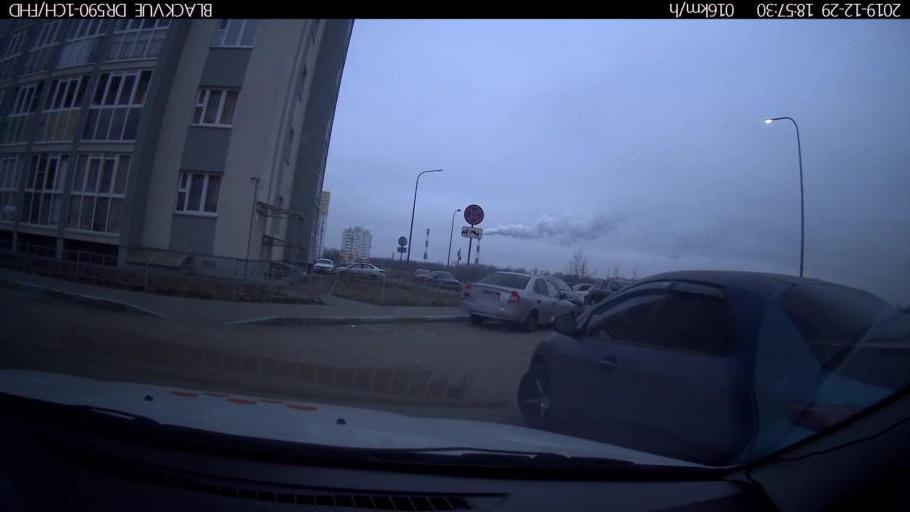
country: RU
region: Nizjnij Novgorod
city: Nizhniy Novgorod
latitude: 56.3436
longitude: 43.9148
